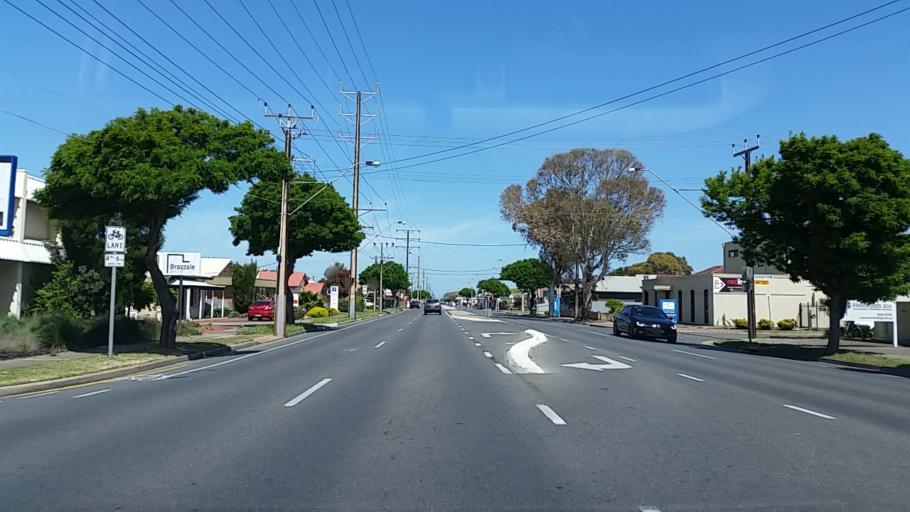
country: AU
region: South Australia
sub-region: Charles Sturt
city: Findon
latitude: -34.9049
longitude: 138.5438
